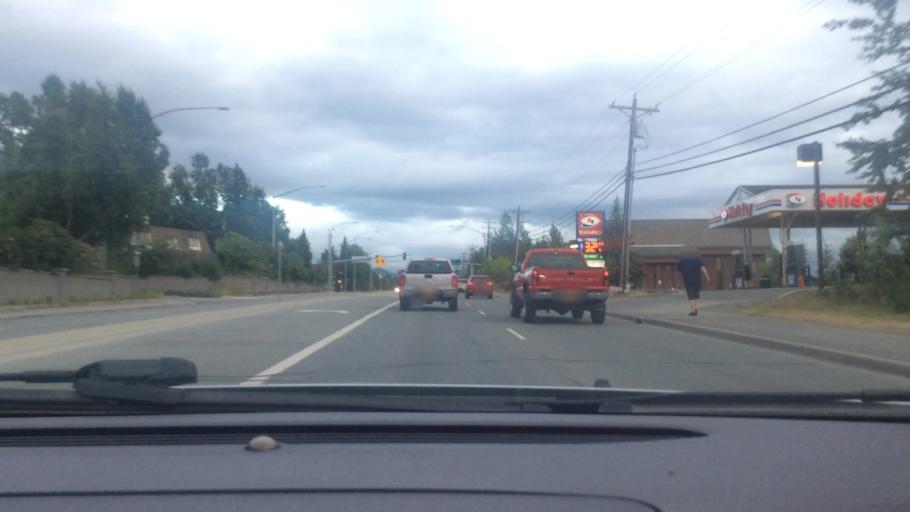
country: US
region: Alaska
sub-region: Anchorage Municipality
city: Elmendorf Air Force Base
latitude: 61.2042
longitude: -149.7335
